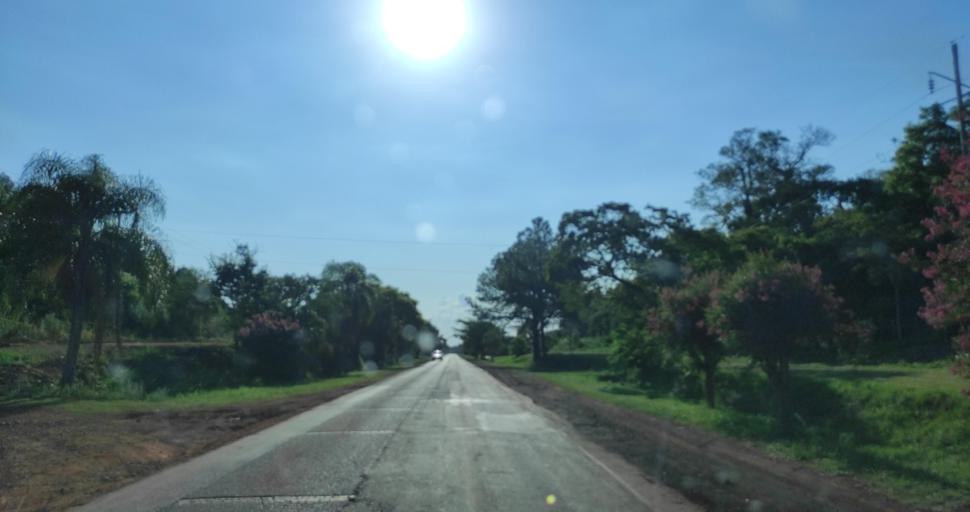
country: AR
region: Misiones
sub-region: Departamento de Eldorado
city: Eldorado
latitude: -26.4002
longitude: -54.4098
